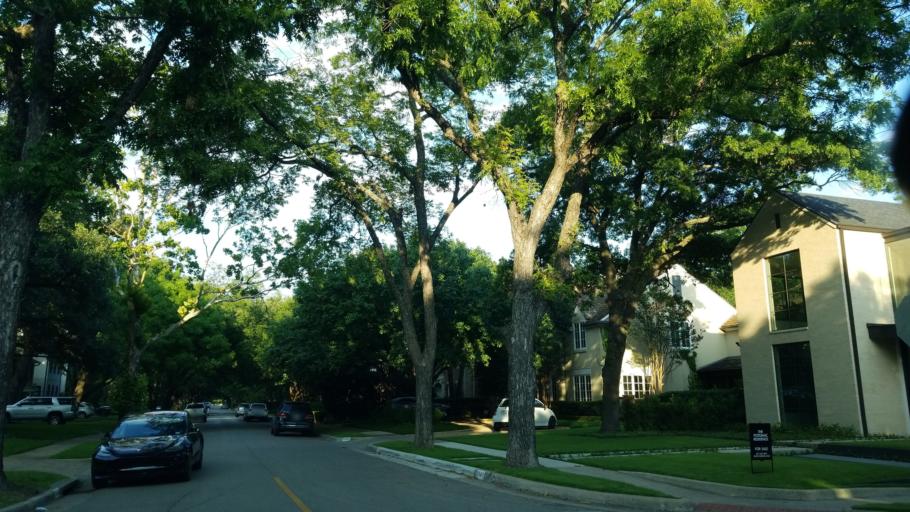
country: US
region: Texas
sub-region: Dallas County
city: Highland Park
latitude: 32.8377
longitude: -96.7920
